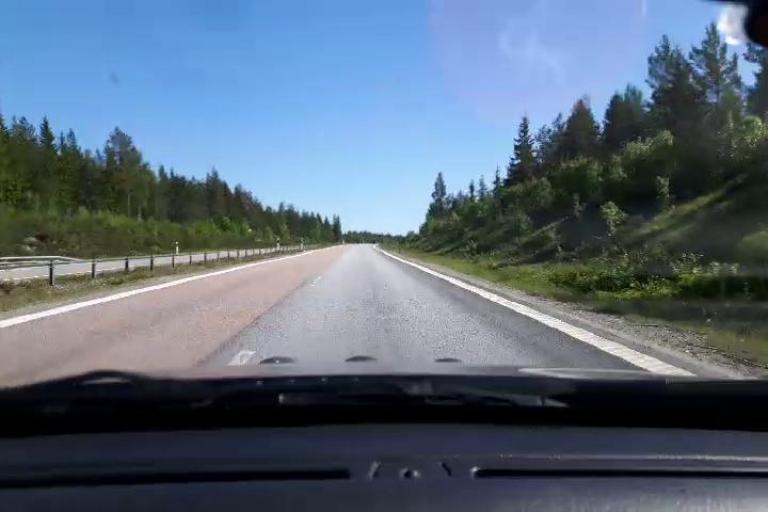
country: SE
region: Gaevleborg
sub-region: Soderhamns Kommun
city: Soderhamn
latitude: 61.3717
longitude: 17.0034
